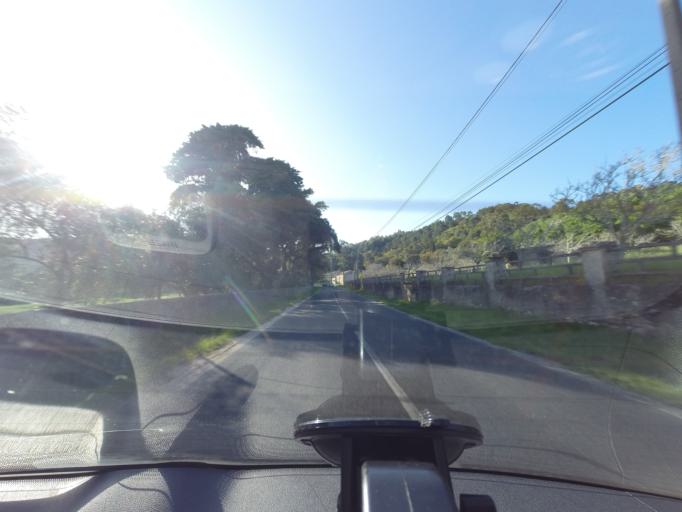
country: PT
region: Lisbon
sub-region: Sintra
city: Sintra
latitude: 38.7672
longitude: -9.3910
